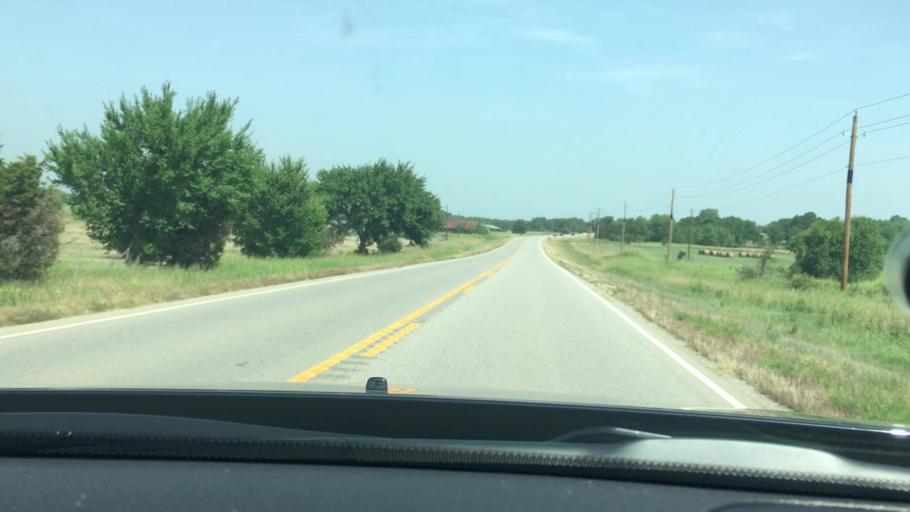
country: US
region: Oklahoma
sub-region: Coal County
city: Coalgate
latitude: 34.4583
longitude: -96.2141
